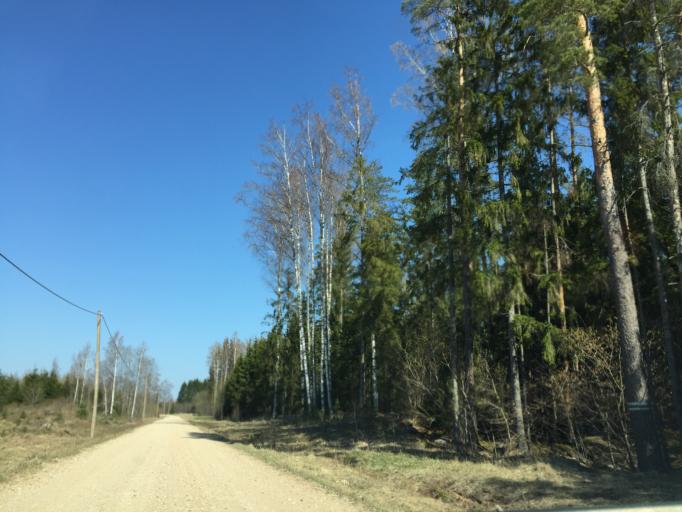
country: EE
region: Tartu
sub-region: Alatskivi vald
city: Kallaste
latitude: 58.5407
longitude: 26.9447
